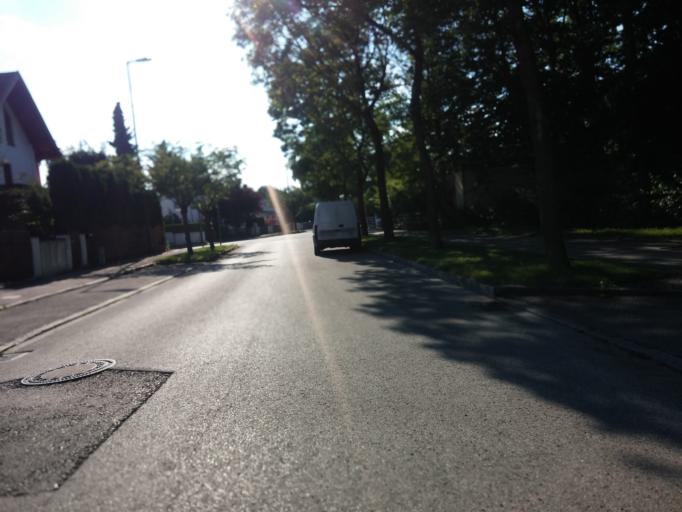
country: DE
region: Bavaria
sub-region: Upper Bavaria
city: Neubiberg
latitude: 48.1302
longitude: 11.6690
